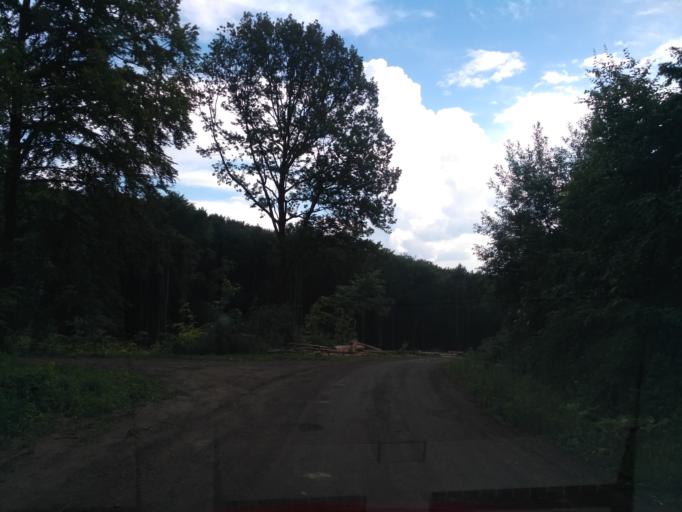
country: SK
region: Presovsky
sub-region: Okres Presov
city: Presov
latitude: 48.9616
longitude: 21.1743
